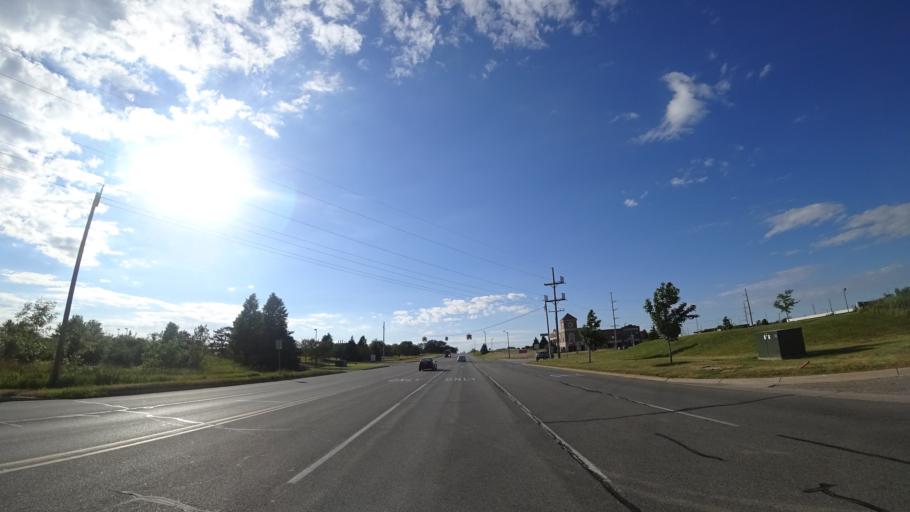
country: US
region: Michigan
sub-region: Ottawa County
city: Holland
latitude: 42.7484
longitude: -86.0763
